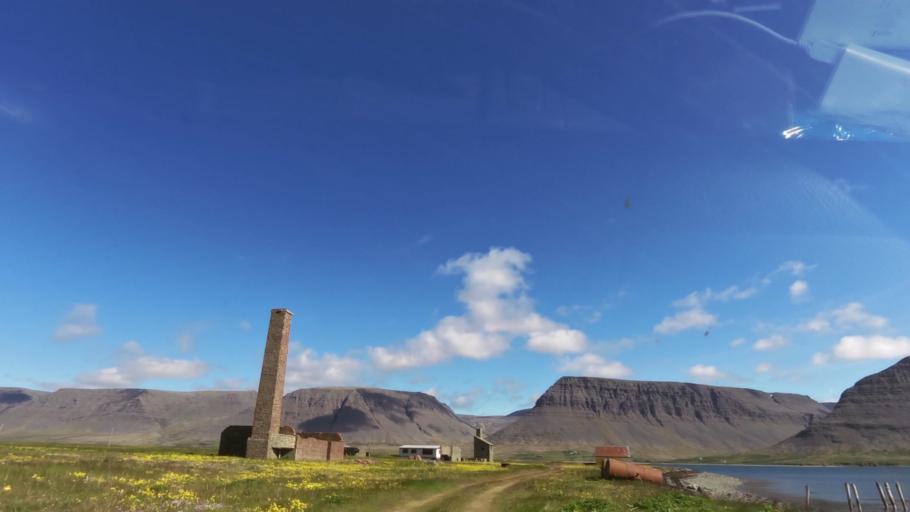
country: IS
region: West
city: Olafsvik
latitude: 65.6389
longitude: -23.9319
